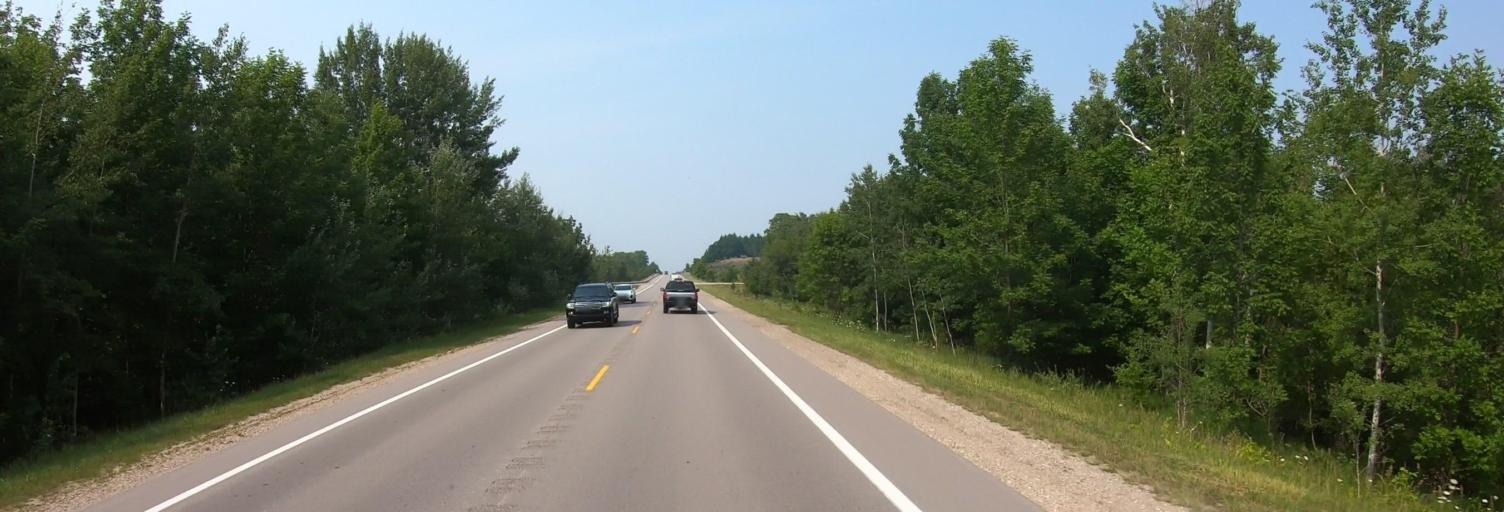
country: US
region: Michigan
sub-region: Charlevoix County
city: Charlevoix
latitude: 45.1414
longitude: -85.3478
